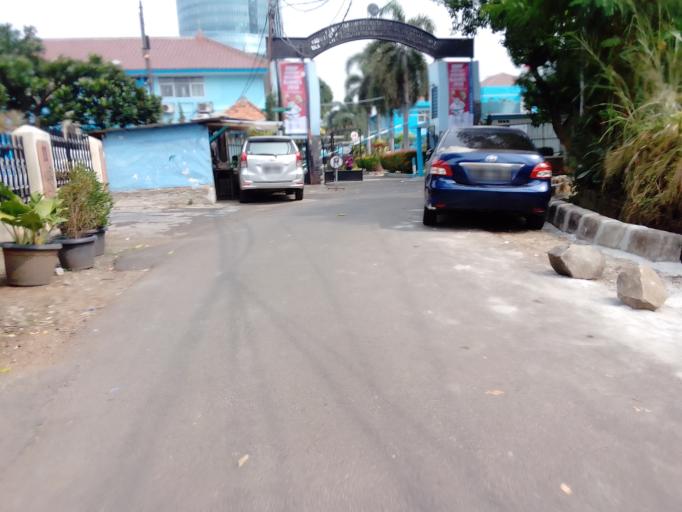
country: ID
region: Jakarta Raya
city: Jakarta
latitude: -6.2012
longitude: 106.8033
